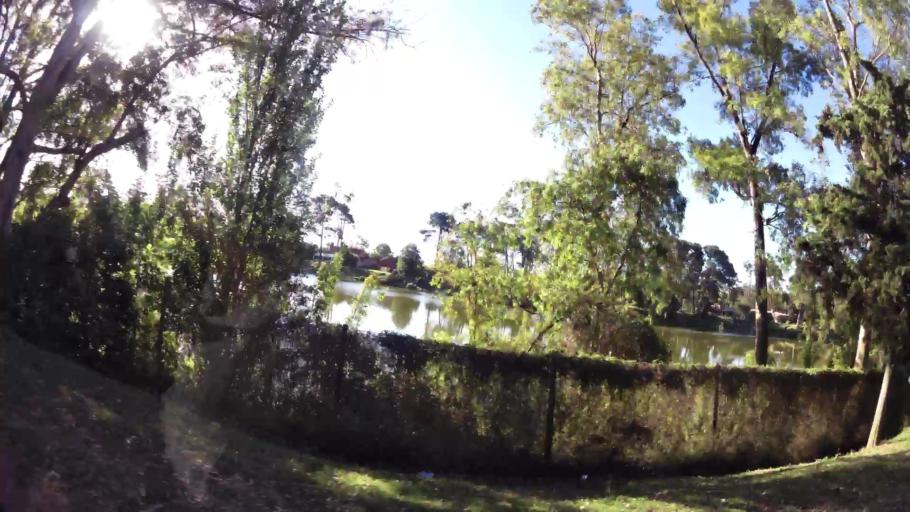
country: UY
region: Canelones
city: Paso de Carrasco
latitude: -34.8571
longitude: -56.0370
